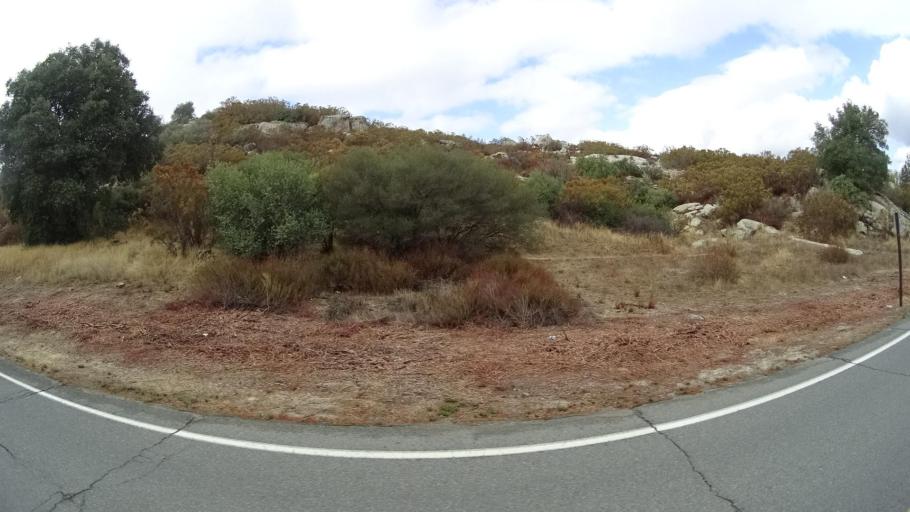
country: US
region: California
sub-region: San Diego County
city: Campo
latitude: 32.6025
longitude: -116.4702
